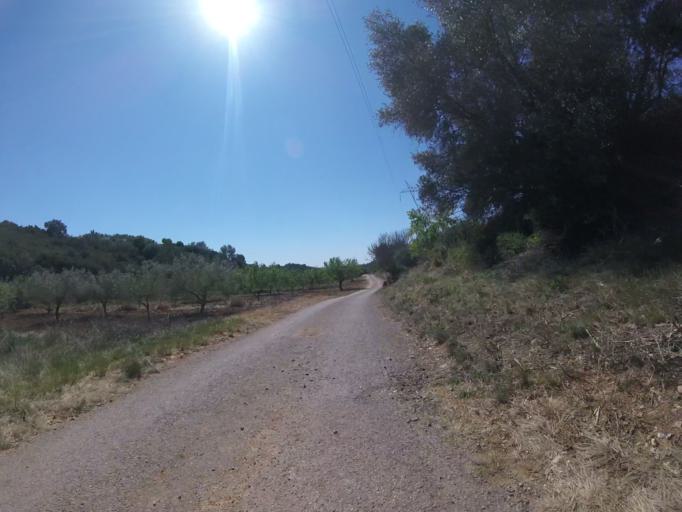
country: ES
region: Valencia
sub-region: Provincia de Castello
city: Cuevas de Vinroma
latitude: 40.3723
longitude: 0.1346
